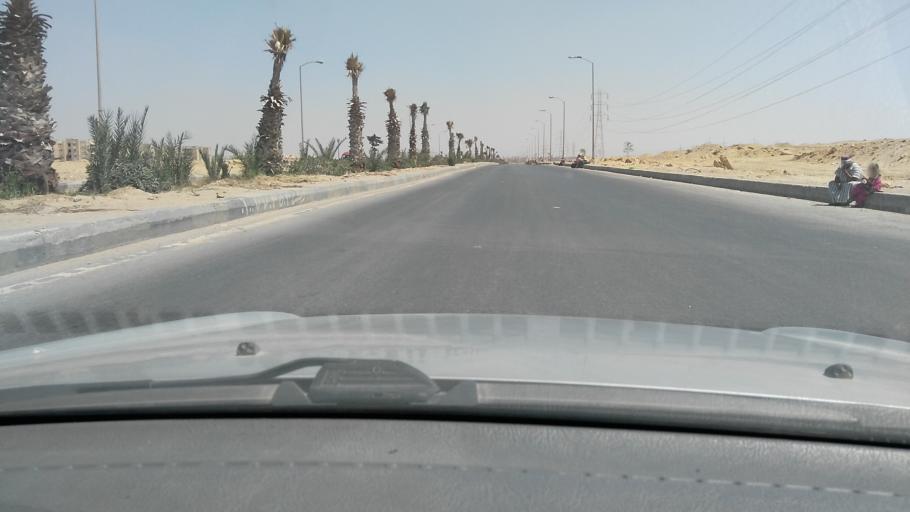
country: EG
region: Al Jizah
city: Madinat Sittah Uktubar
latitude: 29.9343
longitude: 30.9448
